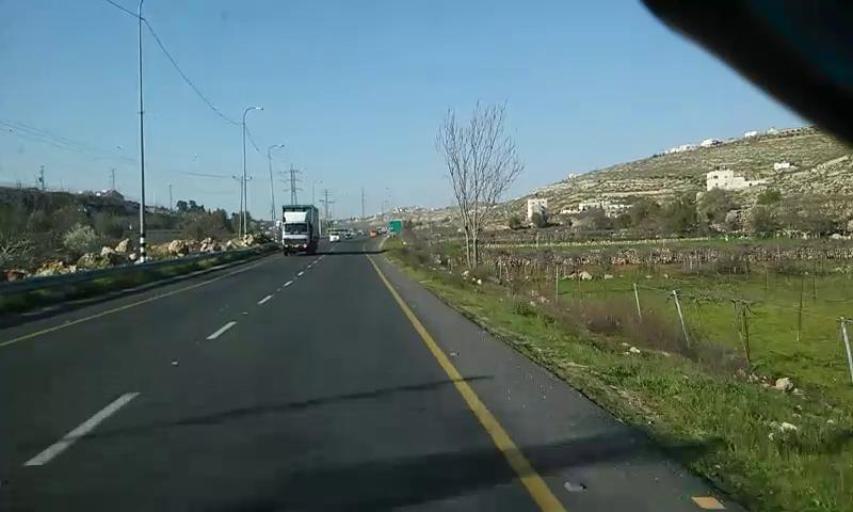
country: PS
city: Al Buq`ah
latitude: 31.5392
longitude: 35.1326
